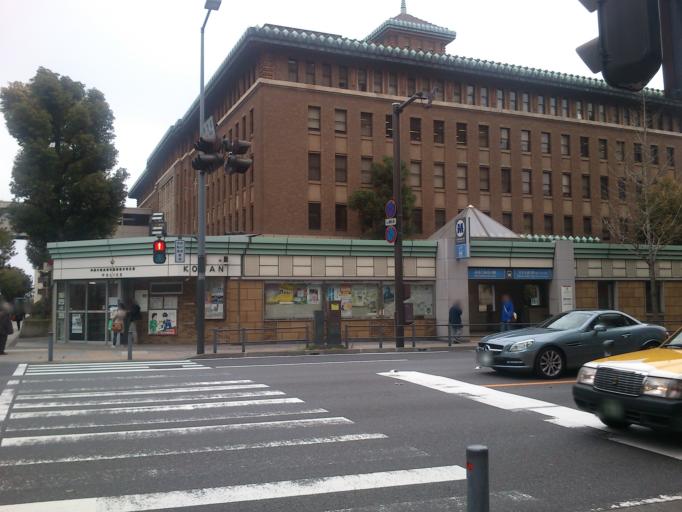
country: JP
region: Kanagawa
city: Yokohama
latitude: 35.4474
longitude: 139.6416
